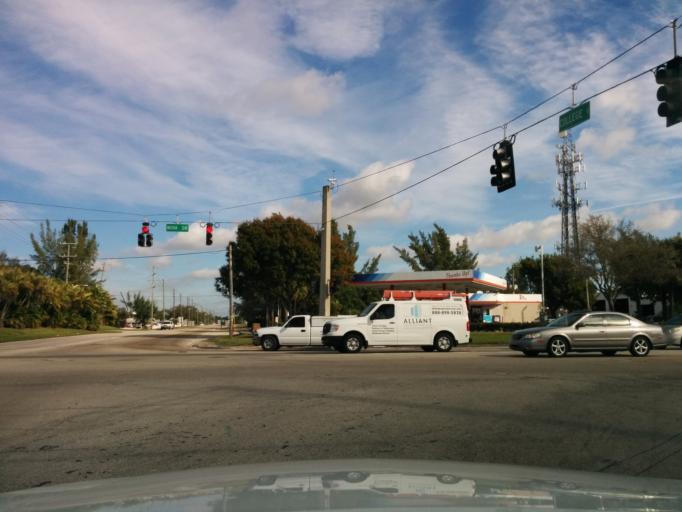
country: US
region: Florida
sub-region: Broward County
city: Davie
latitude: 26.0873
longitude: -80.2361
